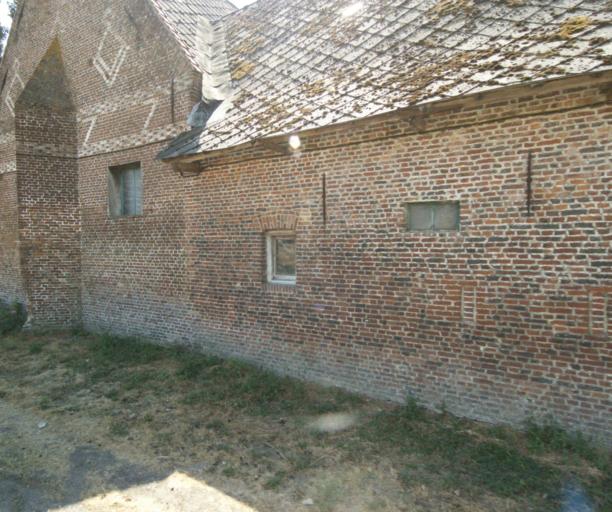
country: FR
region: Nord-Pas-de-Calais
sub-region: Departement du Nord
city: Wervicq-Sud
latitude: 50.7438
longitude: 3.0409
